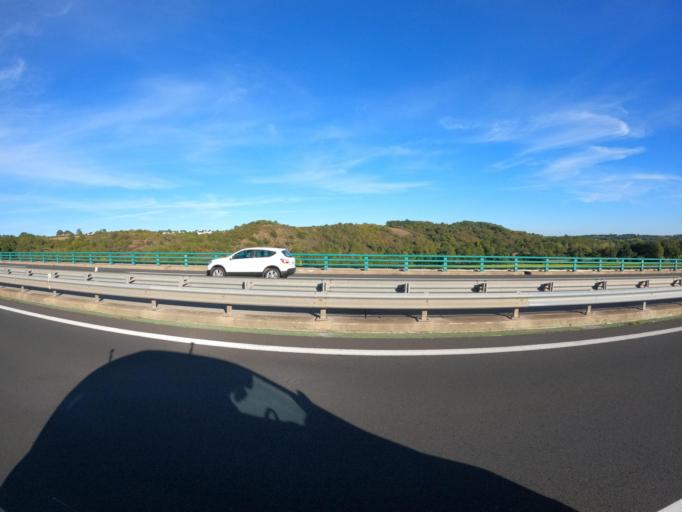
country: FR
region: Pays de la Loire
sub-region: Departement de Maine-et-Loire
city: Beaulieu-sur-Layon
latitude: 47.3105
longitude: -0.6073
